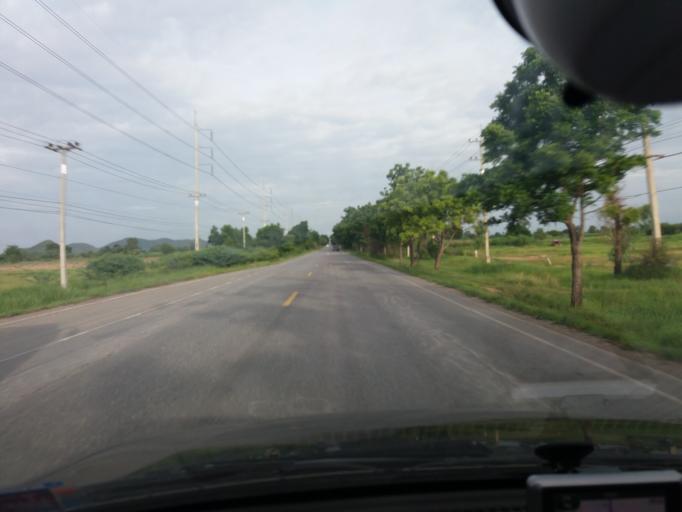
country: TH
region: Kanchanaburi
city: Huai Krachao
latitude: 14.3321
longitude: 99.7325
